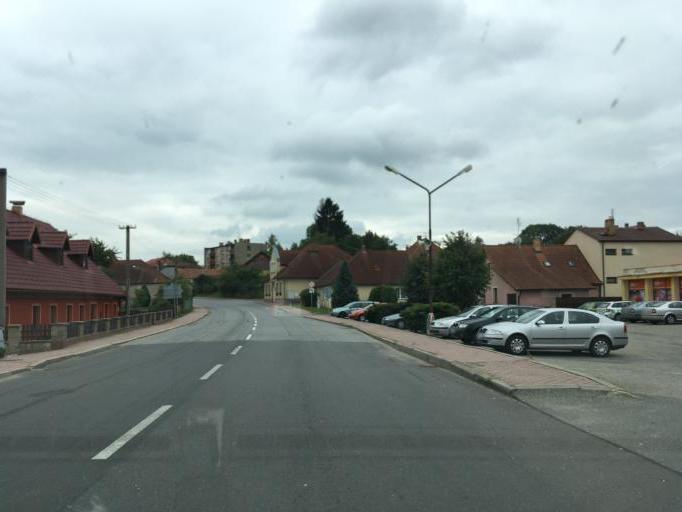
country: CZ
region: Central Bohemia
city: Cechtice
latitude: 49.5580
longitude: 15.1163
